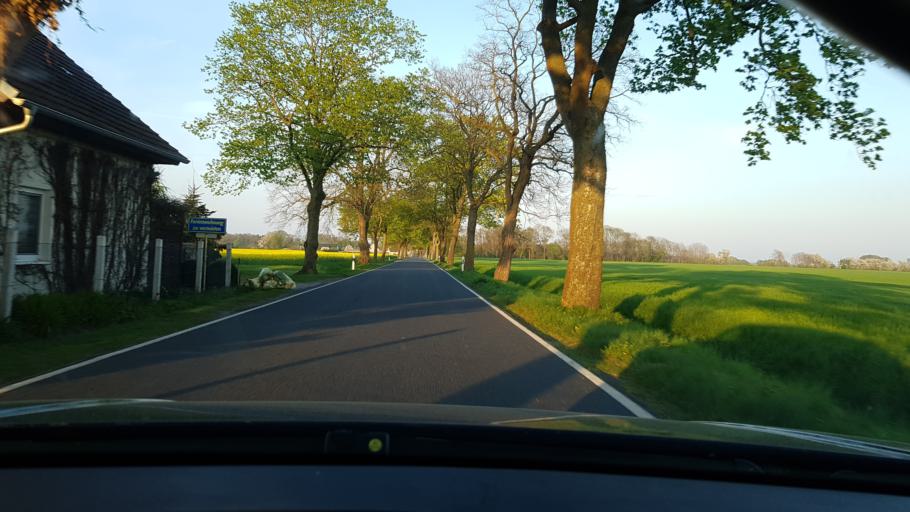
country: DE
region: Mecklenburg-Vorpommern
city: Anklam
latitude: 53.8866
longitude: 13.6587
